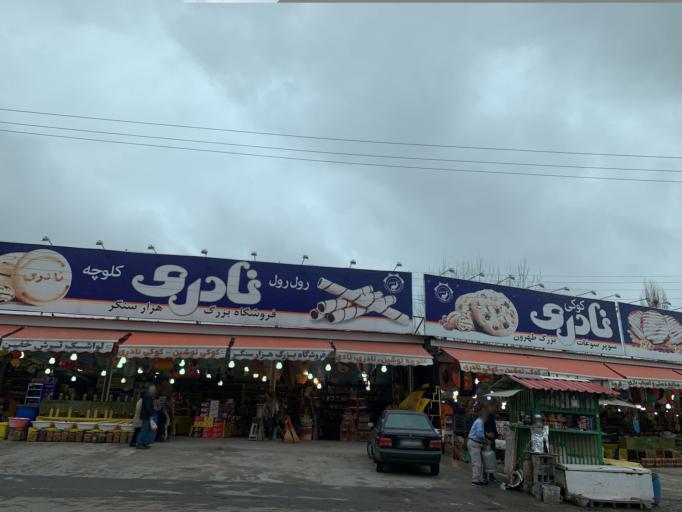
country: IR
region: Mazandaran
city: Amol
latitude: 36.4657
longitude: 52.3938
